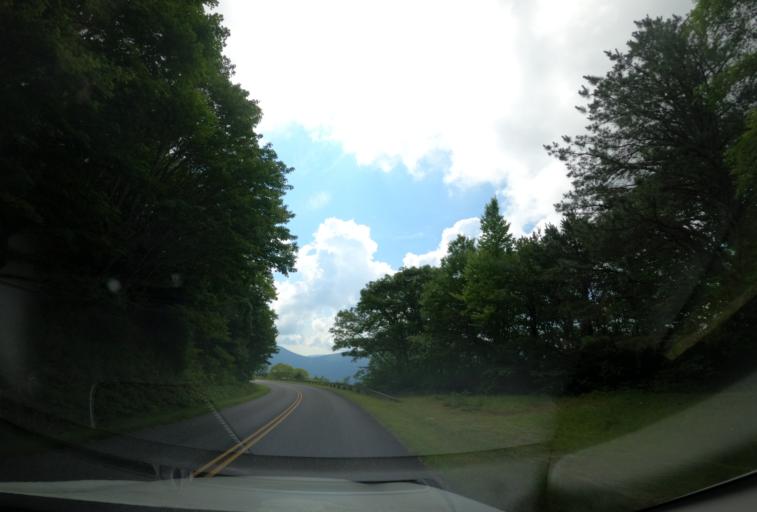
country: US
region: North Carolina
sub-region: Haywood County
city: Hazelwood
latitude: 35.4252
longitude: -83.0380
